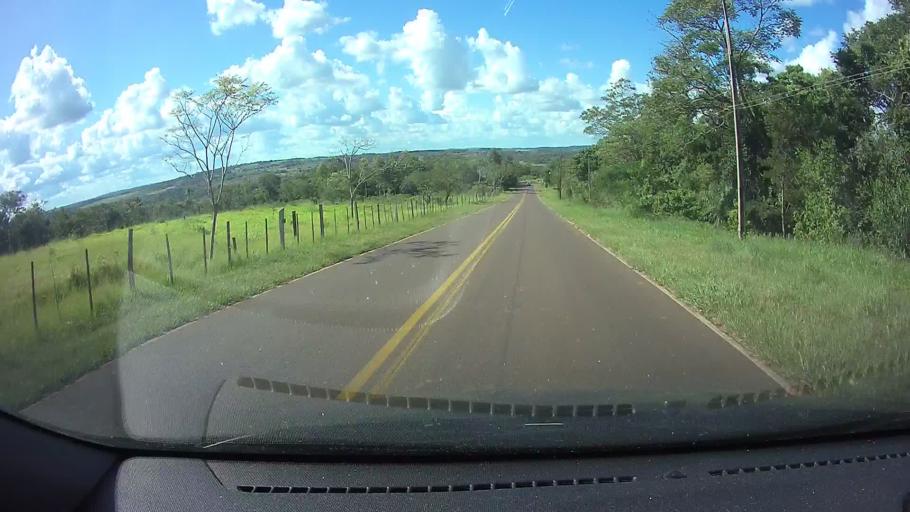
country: PY
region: Paraguari
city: Sapucai
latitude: -25.6435
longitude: -56.8645
